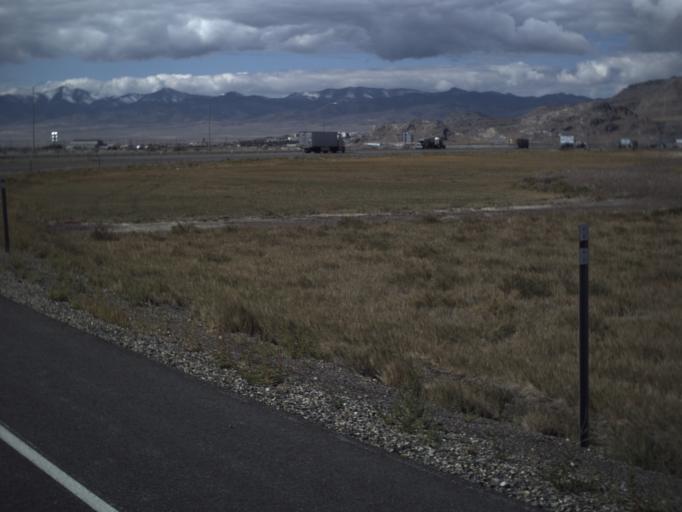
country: US
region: Utah
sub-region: Tooele County
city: Wendover
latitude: 40.7432
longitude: -113.9728
